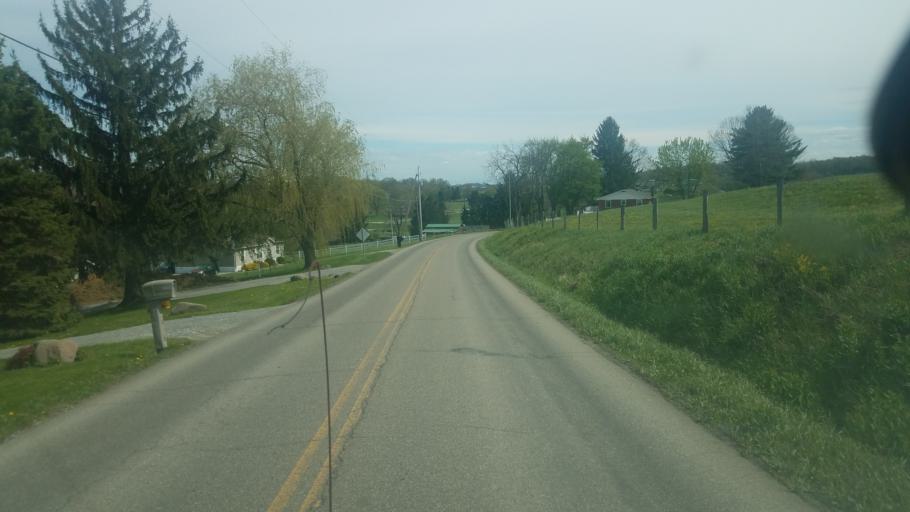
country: US
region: Ohio
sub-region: Holmes County
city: Millersburg
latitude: 40.6122
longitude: -81.8237
